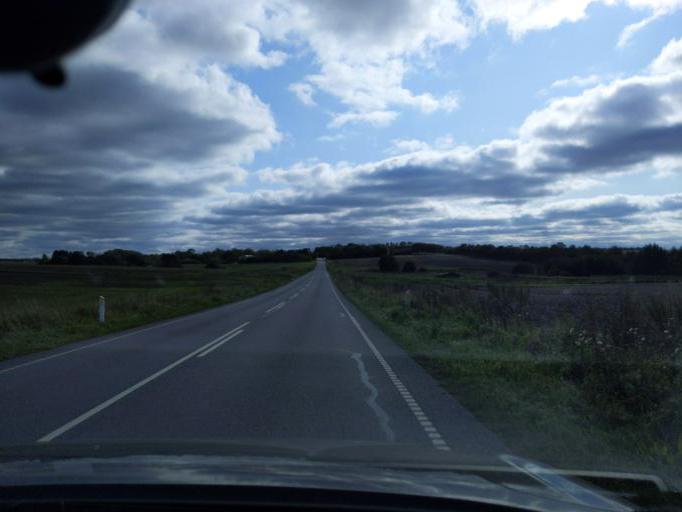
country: DK
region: North Denmark
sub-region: Mariagerfjord Kommune
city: Hobro
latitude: 56.5364
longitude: 9.7257
